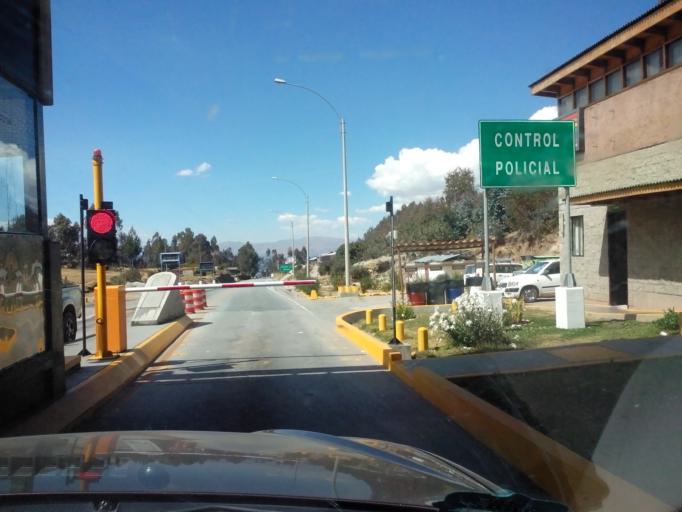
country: PE
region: Cusco
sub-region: Provincia de Anta
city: Ancahuasi
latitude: -13.4419
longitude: -72.3526
